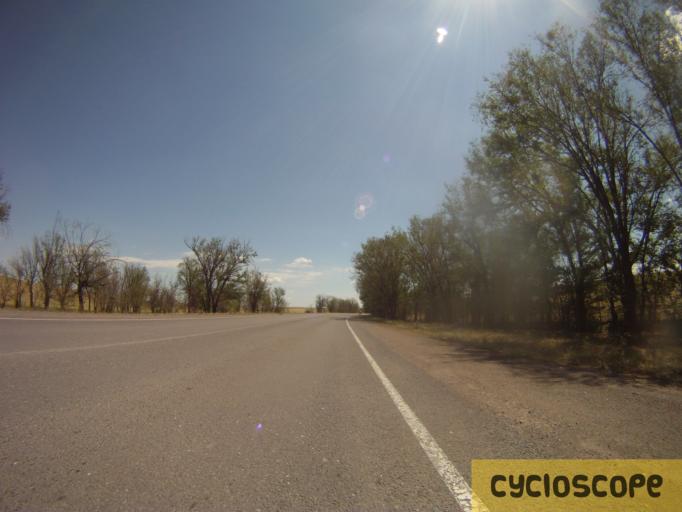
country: KG
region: Chuy
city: Bystrovka
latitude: 43.3251
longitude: 75.9647
